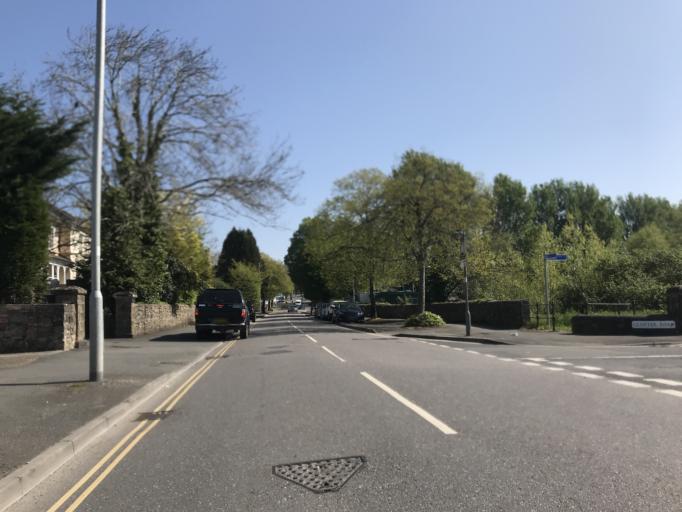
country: GB
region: England
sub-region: Devon
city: Barnstaple
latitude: 51.0753
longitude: -4.0520
